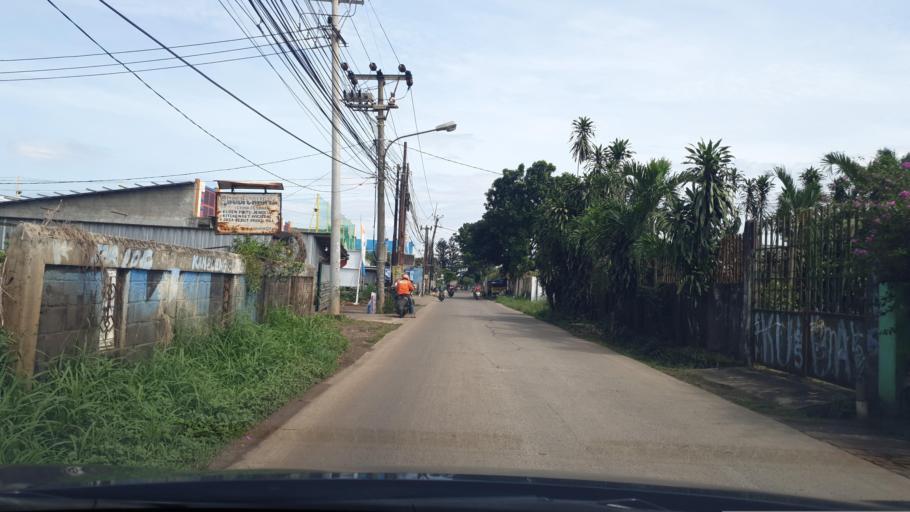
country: ID
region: West Java
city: Sawangan
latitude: -6.4069
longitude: 106.7702
